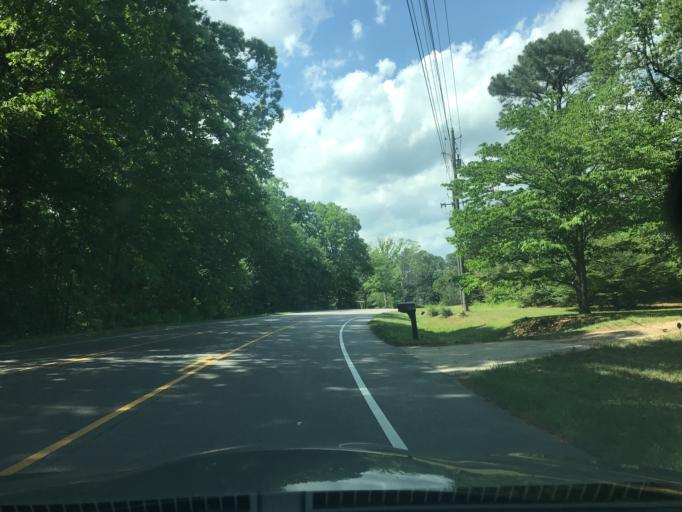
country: US
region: North Carolina
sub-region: Wake County
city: West Raleigh
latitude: 35.8834
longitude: -78.5997
